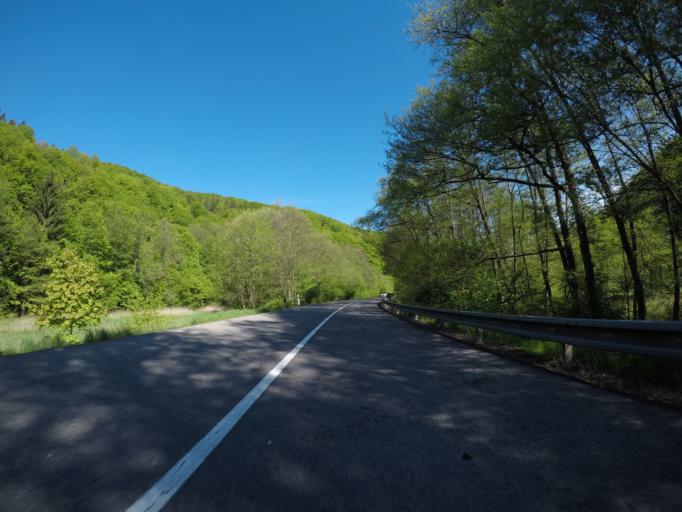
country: SK
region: Banskobystricky
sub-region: Okres Banska Bystrica
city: Banska Stiavnica
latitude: 48.5237
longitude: 19.0047
